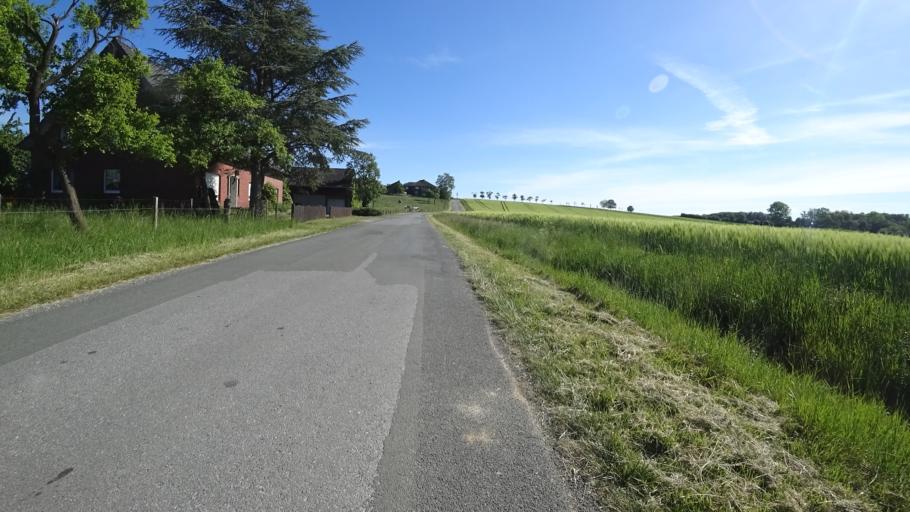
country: DE
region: North Rhine-Westphalia
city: Oelde
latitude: 51.7887
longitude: 8.2014
